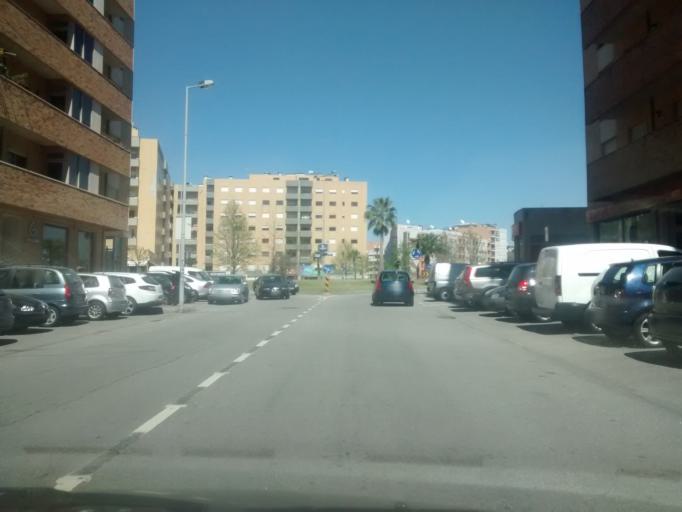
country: PT
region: Braga
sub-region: Braga
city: Braga
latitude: 41.5477
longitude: -8.4032
